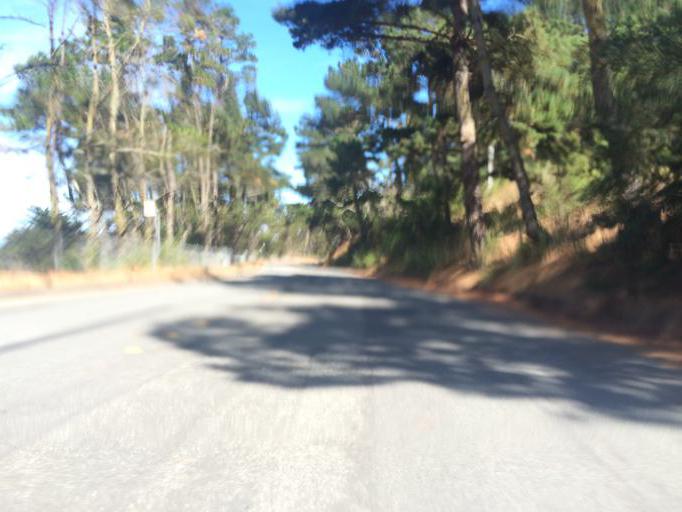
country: US
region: California
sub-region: Monterey County
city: Monterey
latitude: 36.5796
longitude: -121.9042
